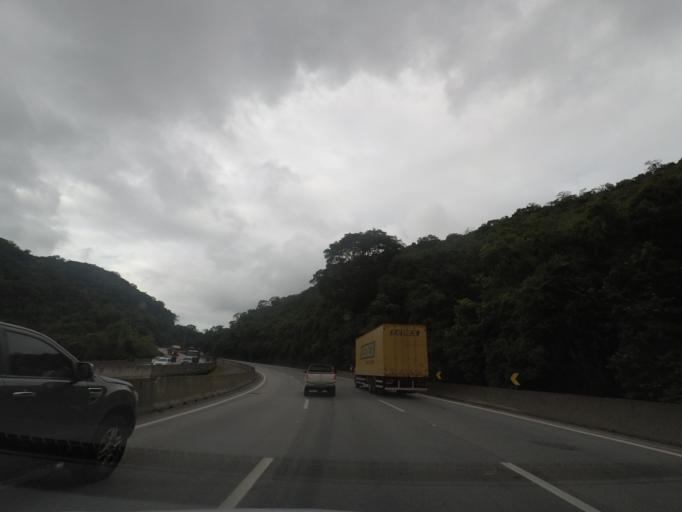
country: BR
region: Sao Paulo
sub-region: Juquitiba
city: Juquitiba
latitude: -24.0516
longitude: -47.2014
